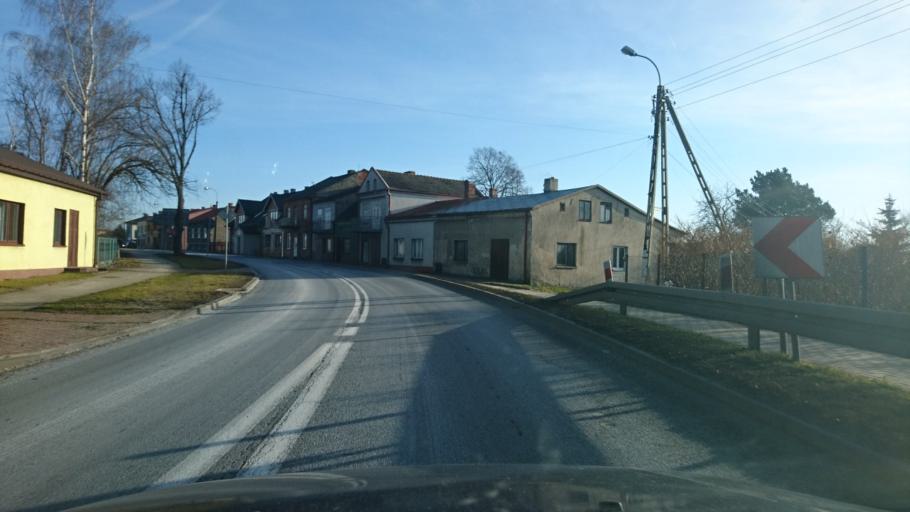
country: PL
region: Opole Voivodeship
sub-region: Powiat oleski
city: Dalachow
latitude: 51.0383
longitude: 18.5986
